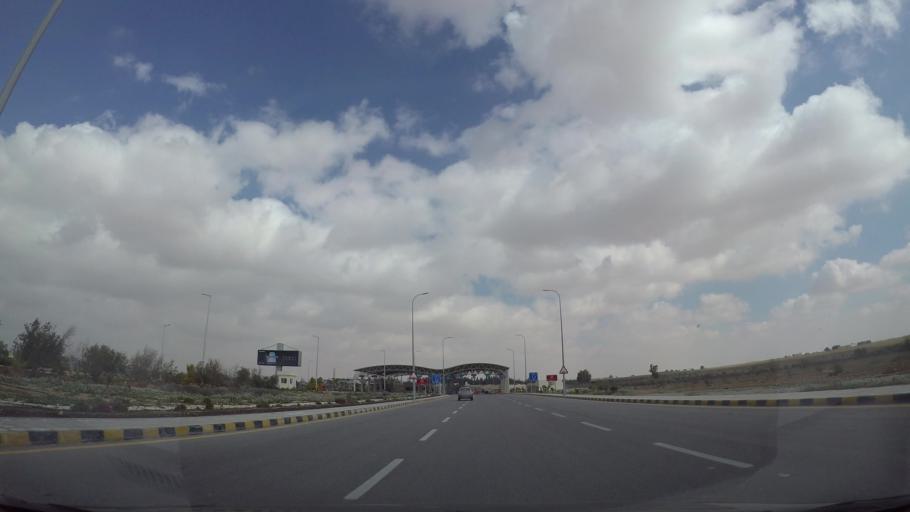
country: JO
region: Amman
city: Al Jizah
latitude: 31.7202
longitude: 35.9697
